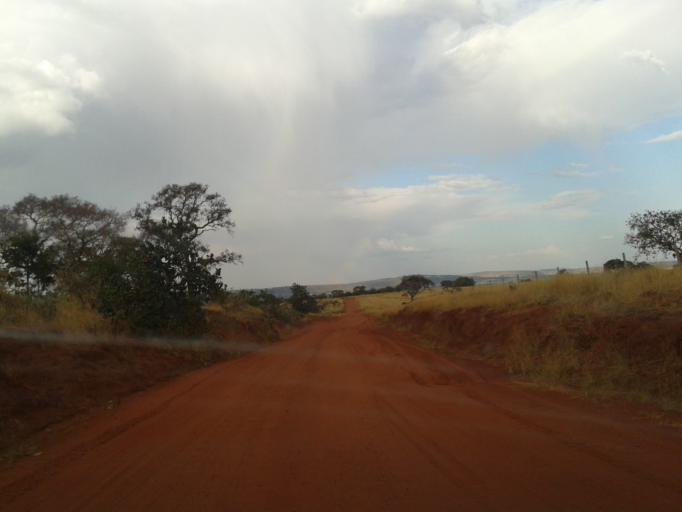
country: BR
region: Minas Gerais
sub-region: Santa Vitoria
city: Santa Vitoria
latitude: -19.1905
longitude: -49.8732
